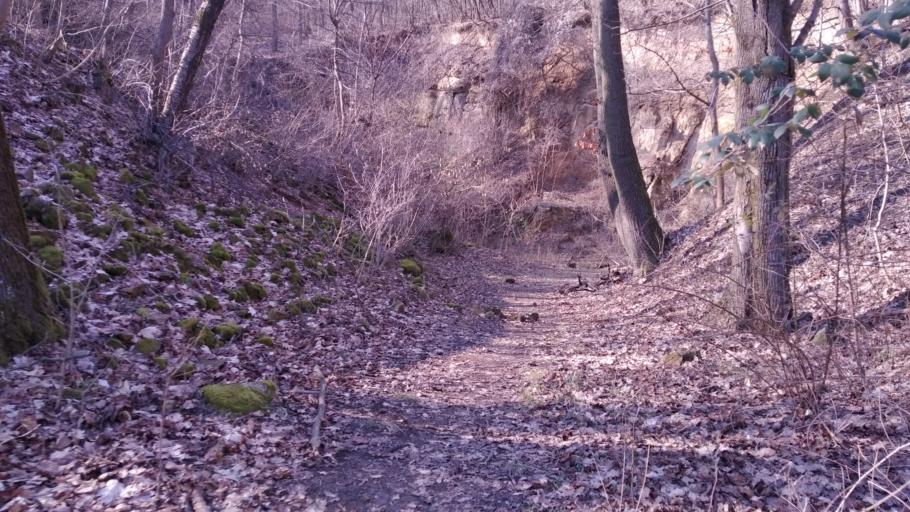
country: HU
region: Pest
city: Pilisborosjeno
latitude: 47.6221
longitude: 19.0001
